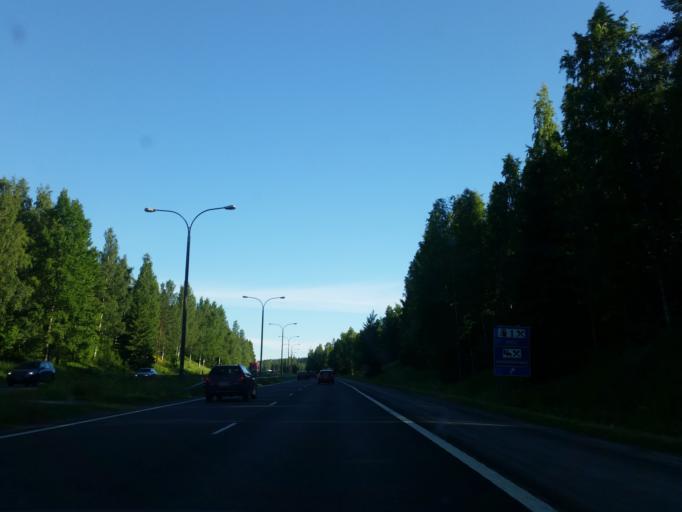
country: FI
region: Northern Savo
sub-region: Kuopio
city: Kuopio
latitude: 62.8701
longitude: 27.6194
